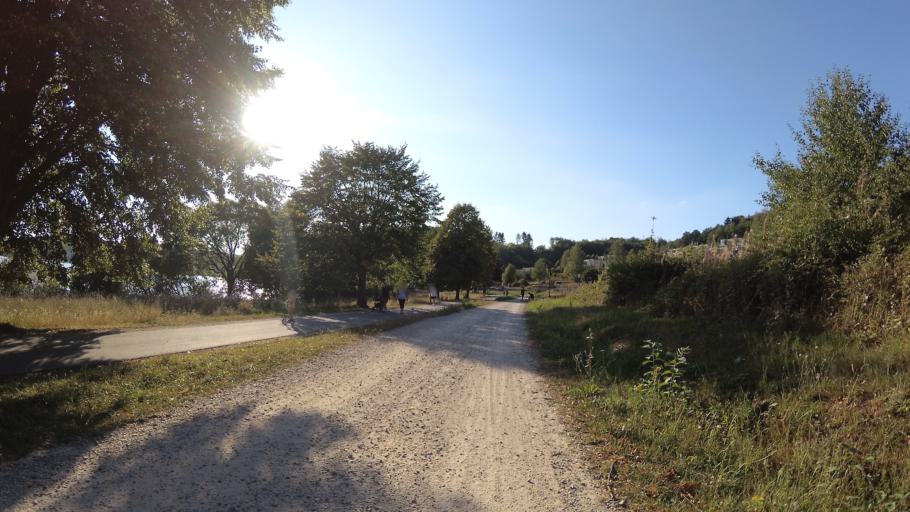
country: DE
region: Rheinland-Pfalz
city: Achtelsbach
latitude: 49.5707
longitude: 7.0757
